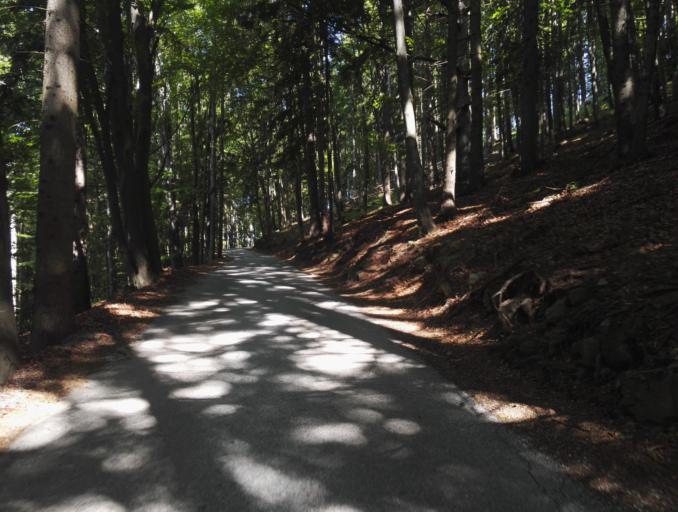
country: AT
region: Styria
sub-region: Politischer Bezirk Graz-Umgebung
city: Stattegg
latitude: 47.1771
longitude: 15.4236
